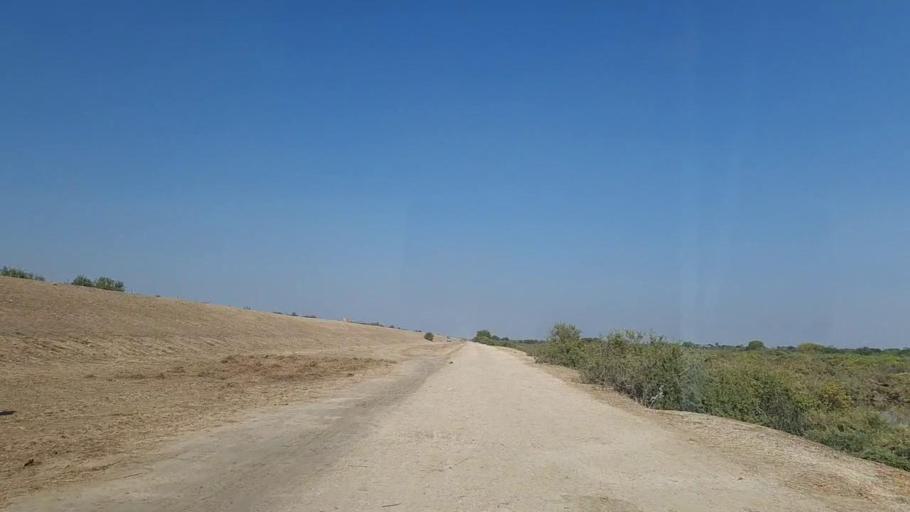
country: PK
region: Sindh
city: Chuhar Jamali
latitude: 24.4597
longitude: 68.0019
